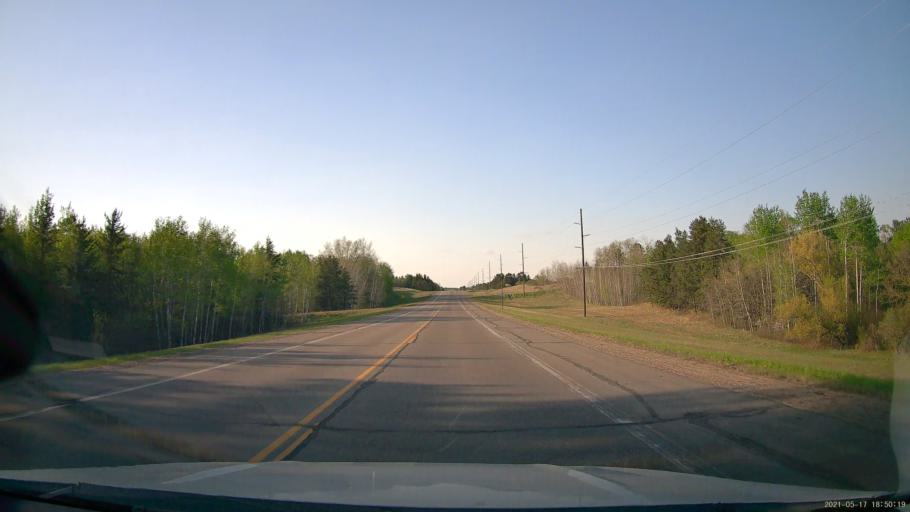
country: US
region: Minnesota
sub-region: Hubbard County
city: Park Rapids
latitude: 46.9325
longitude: -95.0168
